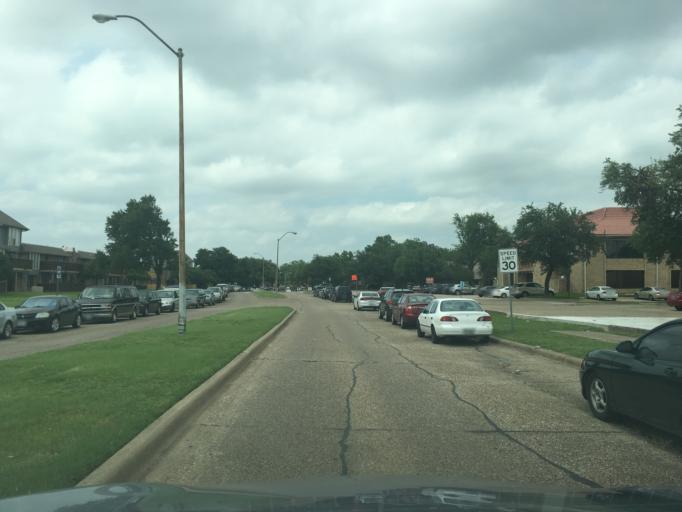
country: US
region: Texas
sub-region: Dallas County
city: Richardson
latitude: 32.9405
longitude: -96.7640
